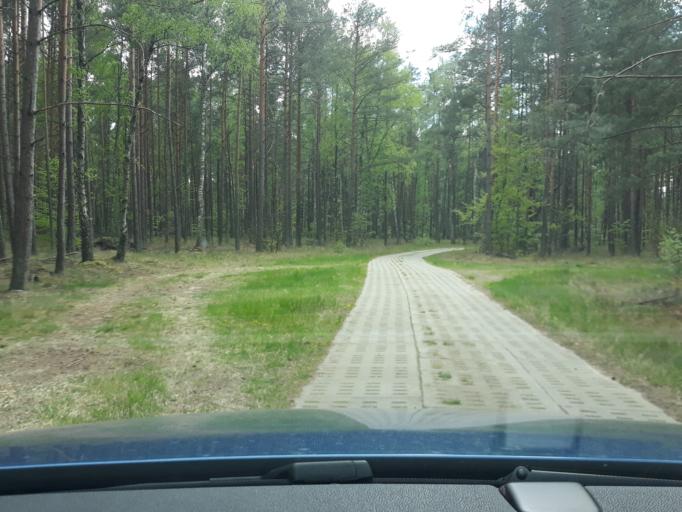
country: PL
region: Pomeranian Voivodeship
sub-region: Powiat czluchowski
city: Przechlewo
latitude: 53.7498
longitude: 17.3179
